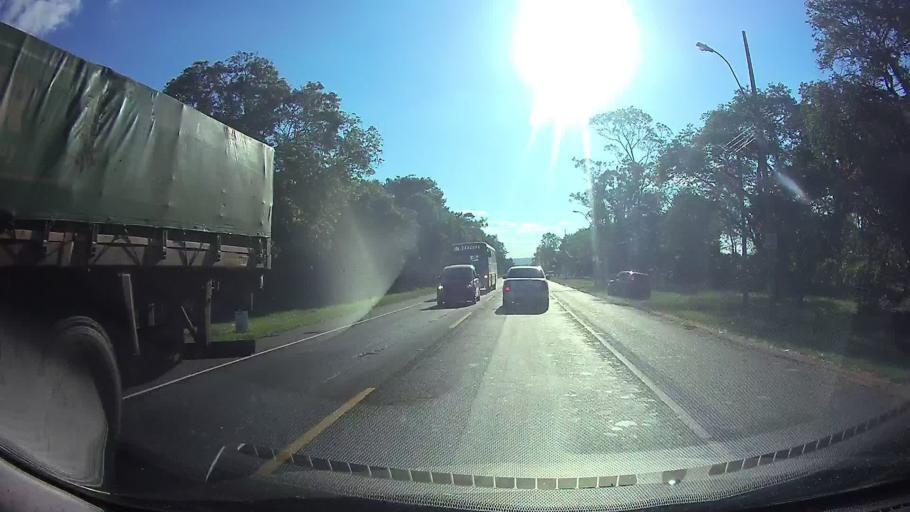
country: PY
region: Central
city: Ypacarai
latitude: -25.3746
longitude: -57.2273
